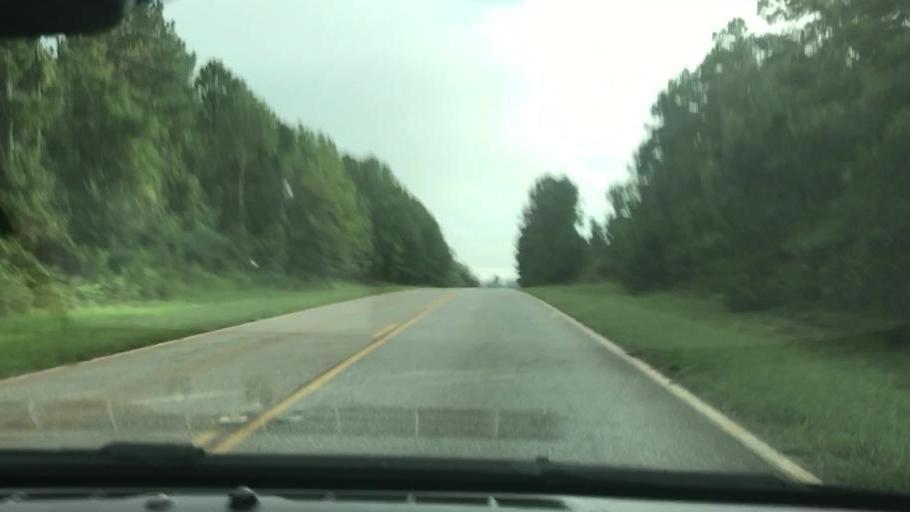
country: US
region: Georgia
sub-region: Quitman County
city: Georgetown
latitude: 31.9169
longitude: -85.0266
